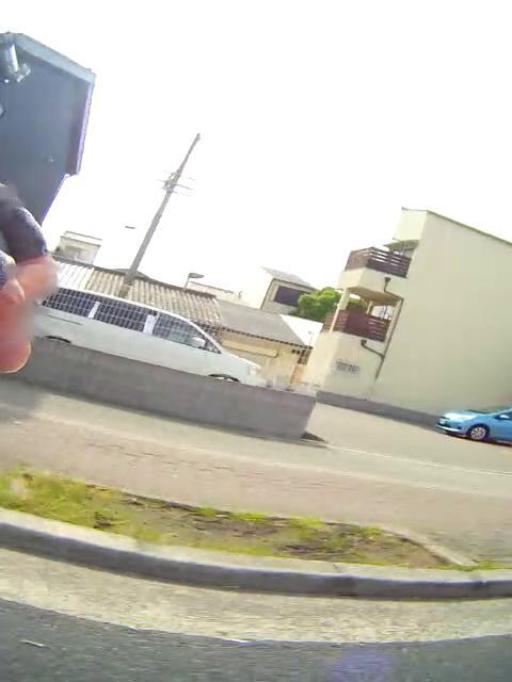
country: JP
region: Osaka
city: Osaka-shi
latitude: 34.6611
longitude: 135.5418
